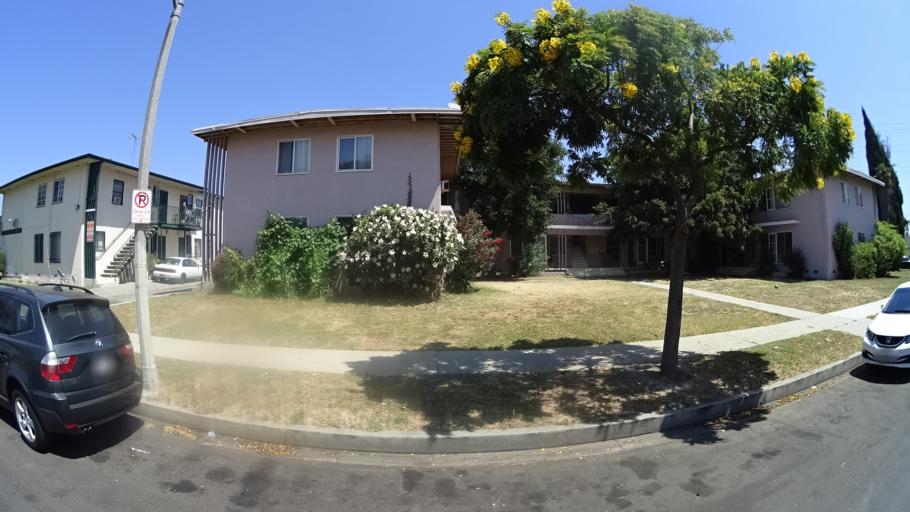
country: US
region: California
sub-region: Los Angeles County
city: Culver City
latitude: 34.0248
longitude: -118.3673
